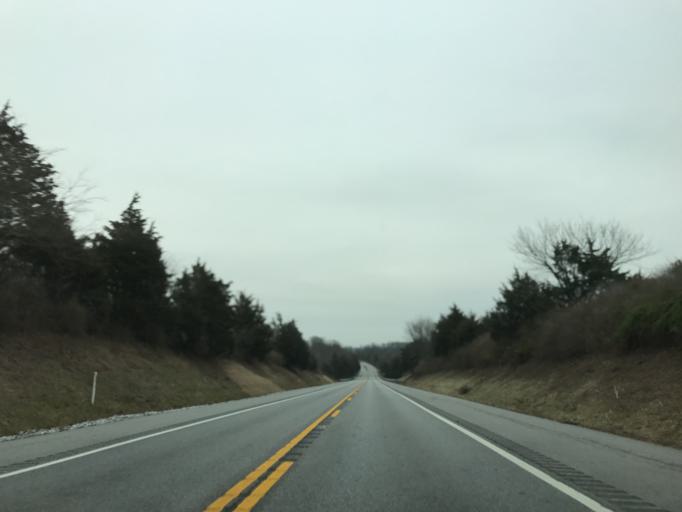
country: US
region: Maryland
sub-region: Carroll County
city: Taneytown
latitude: 39.6412
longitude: -77.1272
